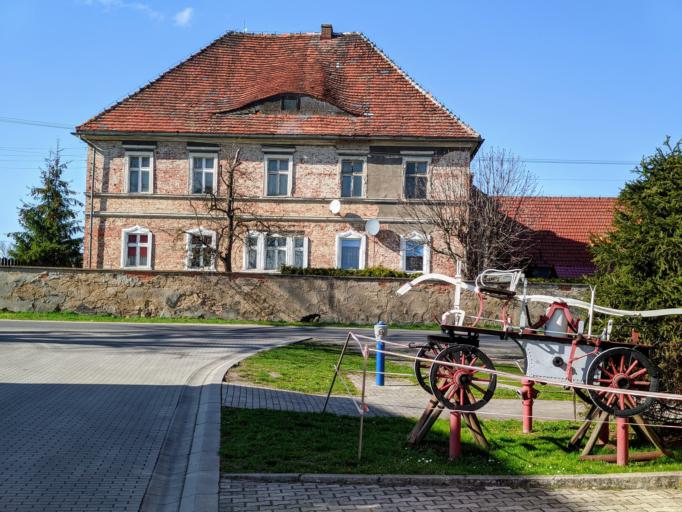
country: PL
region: Lubusz
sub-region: Powiat zarski
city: Zary
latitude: 51.7191
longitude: 15.1800
